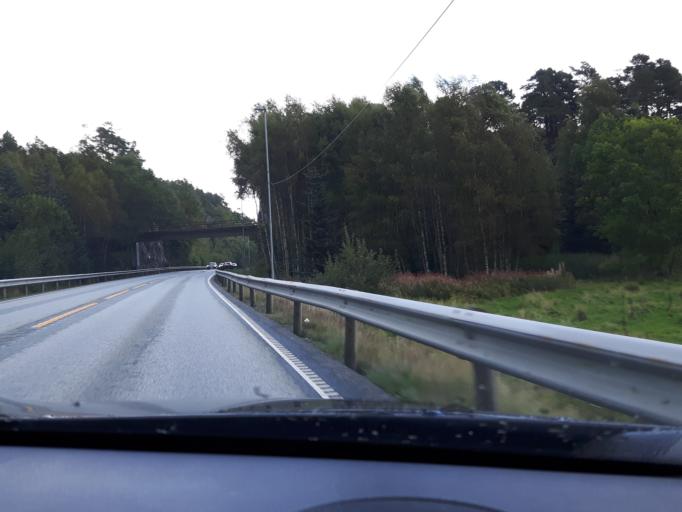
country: NO
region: Vest-Agder
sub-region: Sogne
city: Tangvall
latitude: 58.0967
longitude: 7.8034
